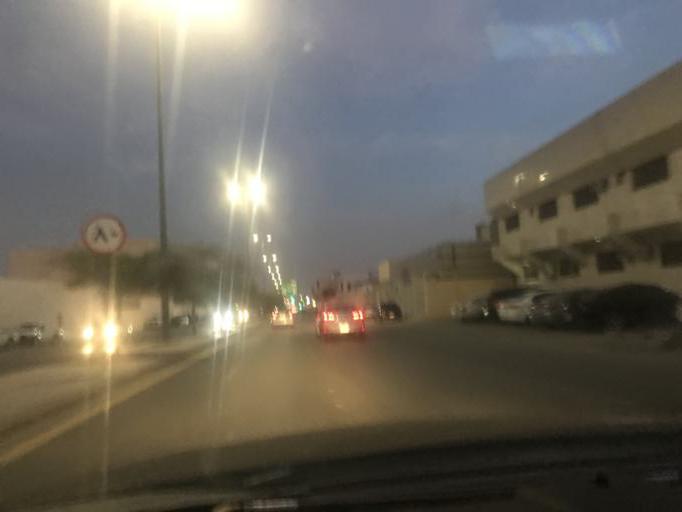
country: SA
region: Ar Riyad
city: Riyadh
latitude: 24.7341
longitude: 46.7599
